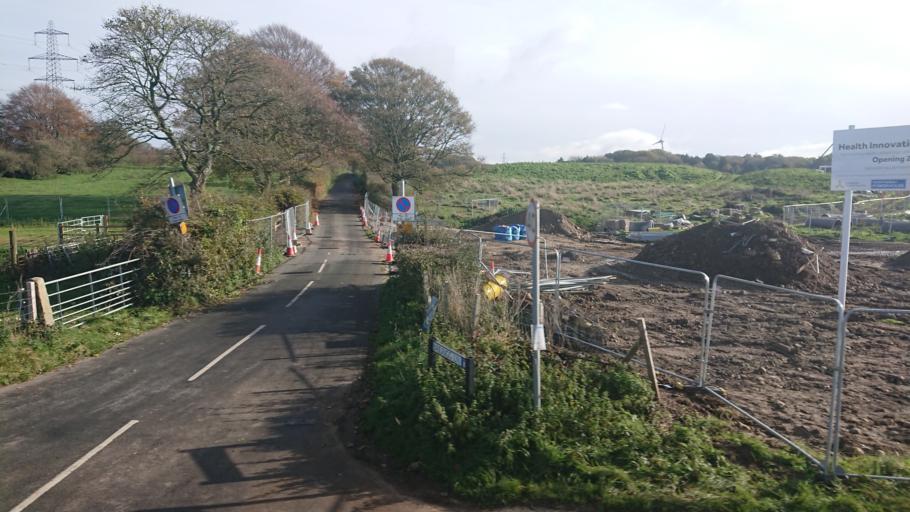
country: GB
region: England
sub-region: Lancashire
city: Lancaster
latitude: 54.0178
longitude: -2.7966
